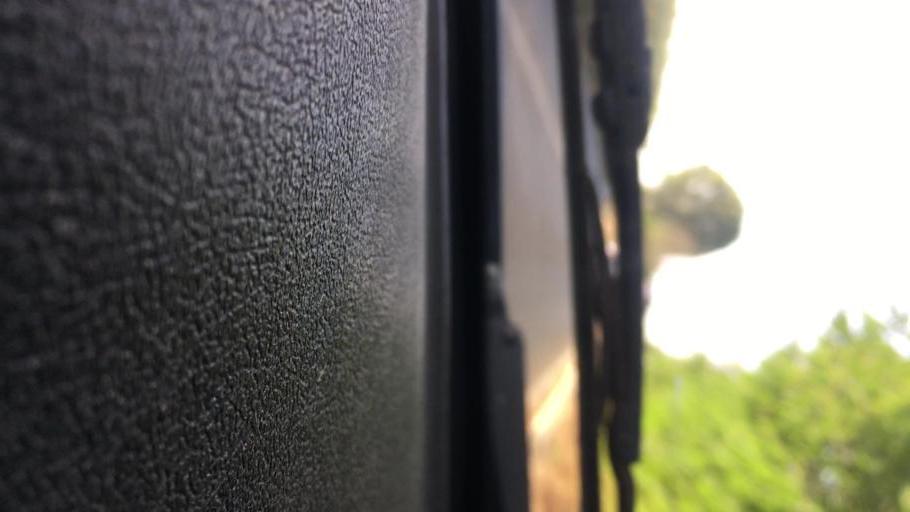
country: IT
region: Latium
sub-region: Citta metropolitana di Roma Capitale
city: Borgo Lotti
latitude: 41.8060
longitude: 12.5338
